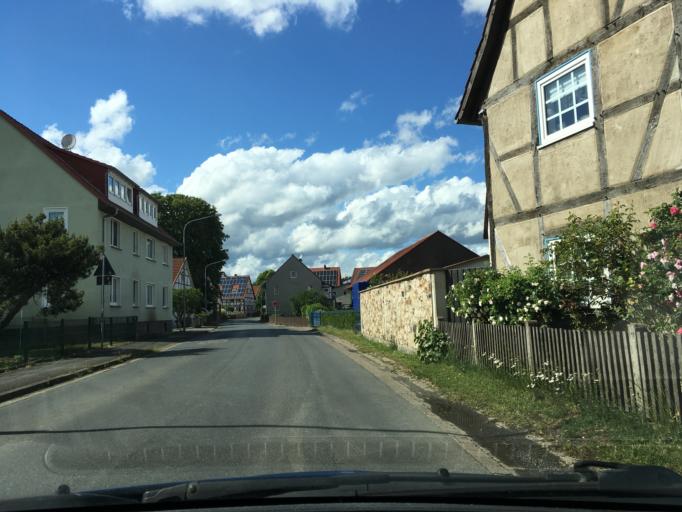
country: DE
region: Lower Saxony
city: Bovenden
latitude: 51.5835
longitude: 9.8745
